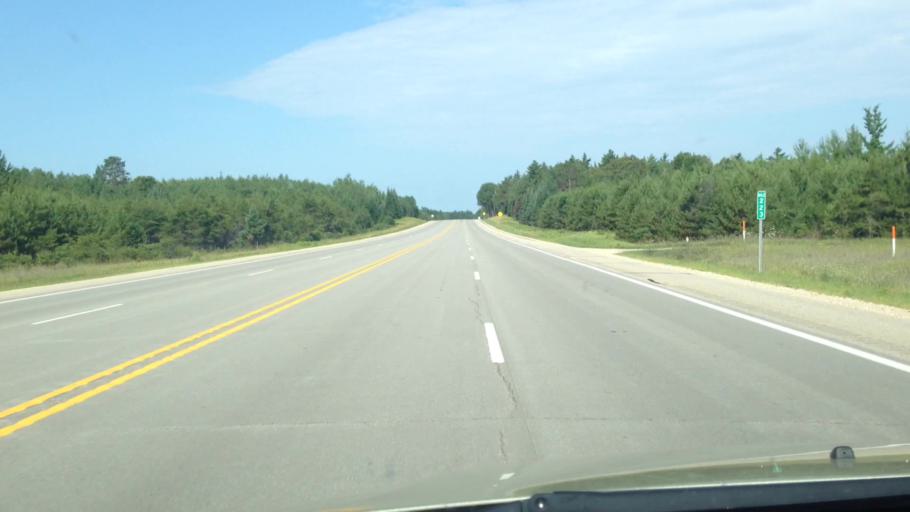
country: US
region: Michigan
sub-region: Schoolcraft County
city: Manistique
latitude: 45.9081
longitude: -86.4272
